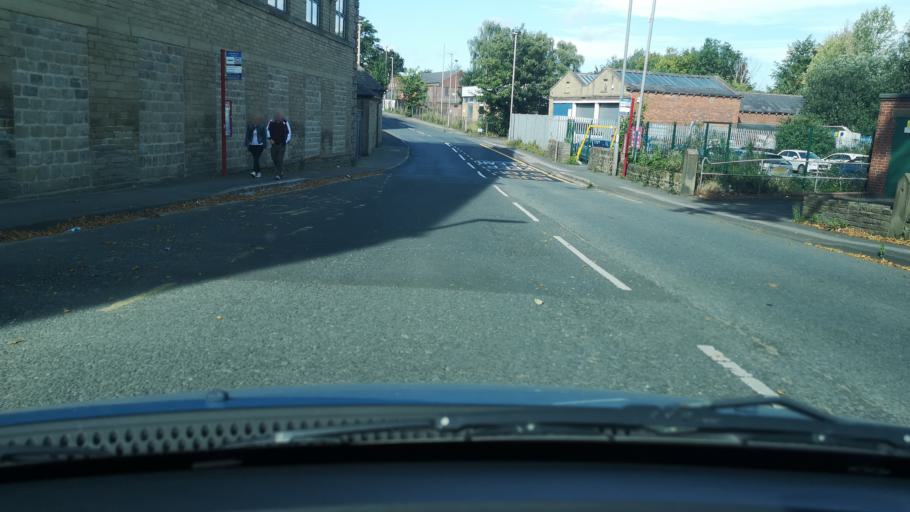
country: GB
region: England
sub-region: Kirklees
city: Batley
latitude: 53.7152
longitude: -1.6376
